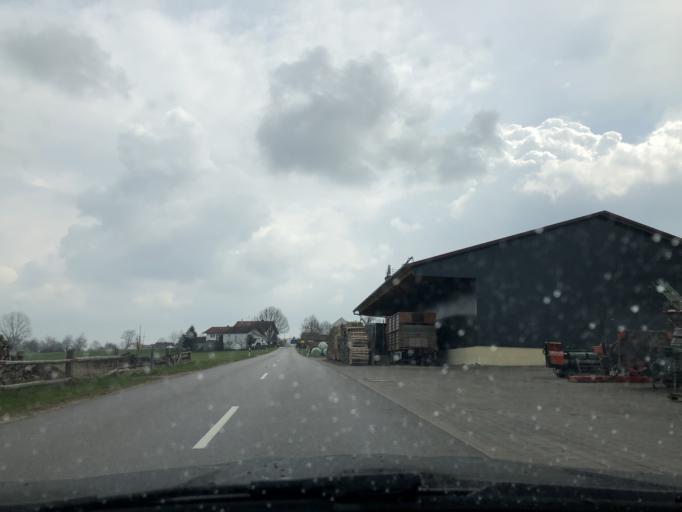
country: DE
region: Bavaria
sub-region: Upper Bavaria
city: Wolfersdorf
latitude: 48.4851
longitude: 11.7008
